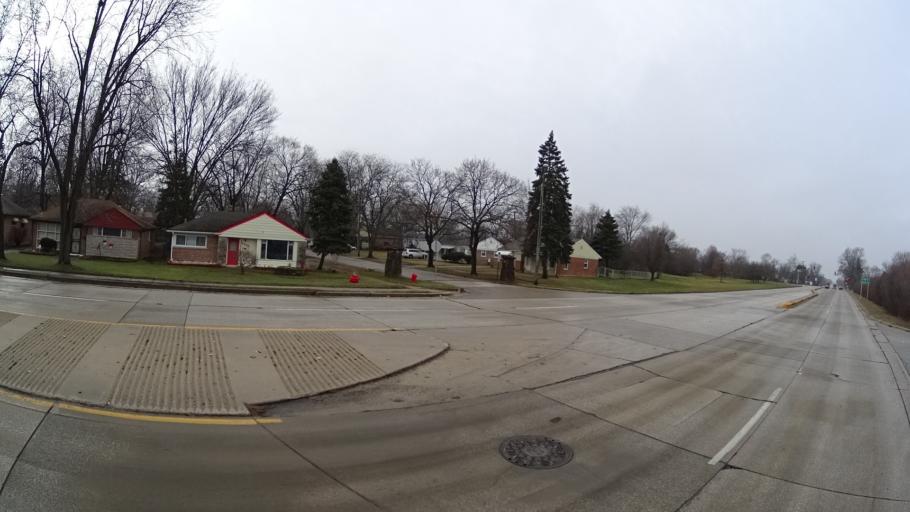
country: US
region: Illinois
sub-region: Cook County
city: Hazel Crest
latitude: 41.5719
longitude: -87.6774
